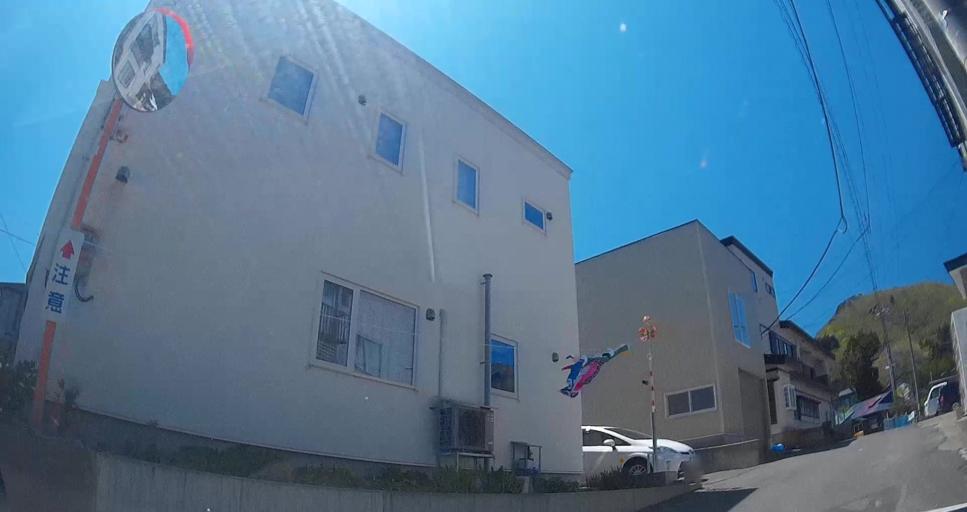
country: JP
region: Aomori
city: Mutsu
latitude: 41.3723
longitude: 141.4488
